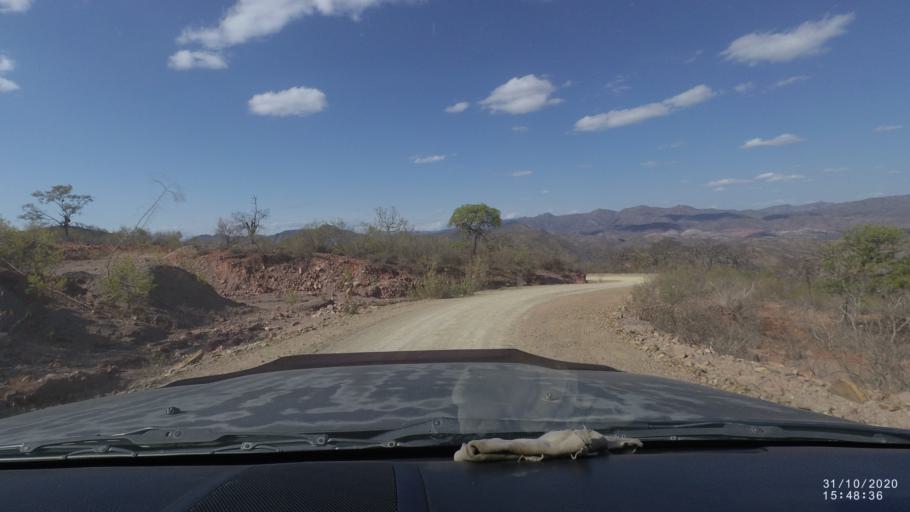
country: BO
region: Chuquisaca
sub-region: Provincia Zudanez
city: Mojocoya
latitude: -18.3110
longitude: -64.7103
